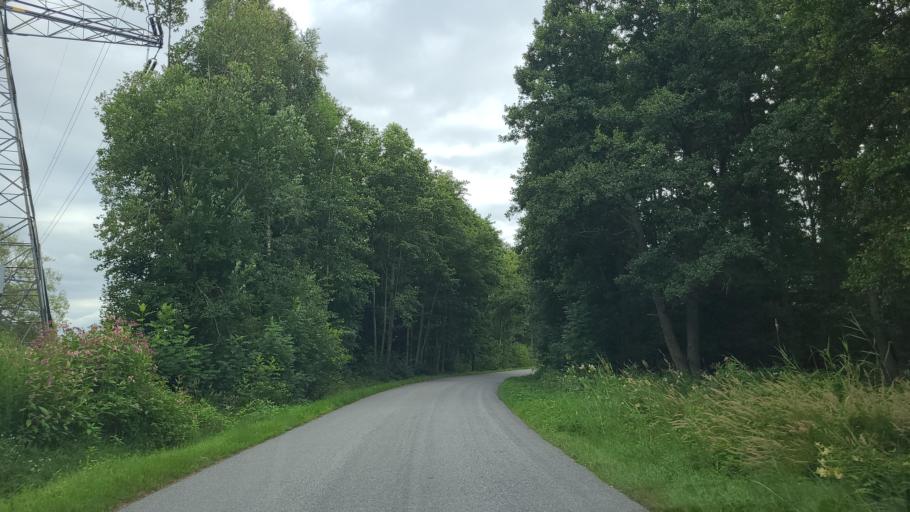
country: SE
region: Stockholm
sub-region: Upplands-Bro Kommun
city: Bro
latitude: 59.4776
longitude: 17.5617
